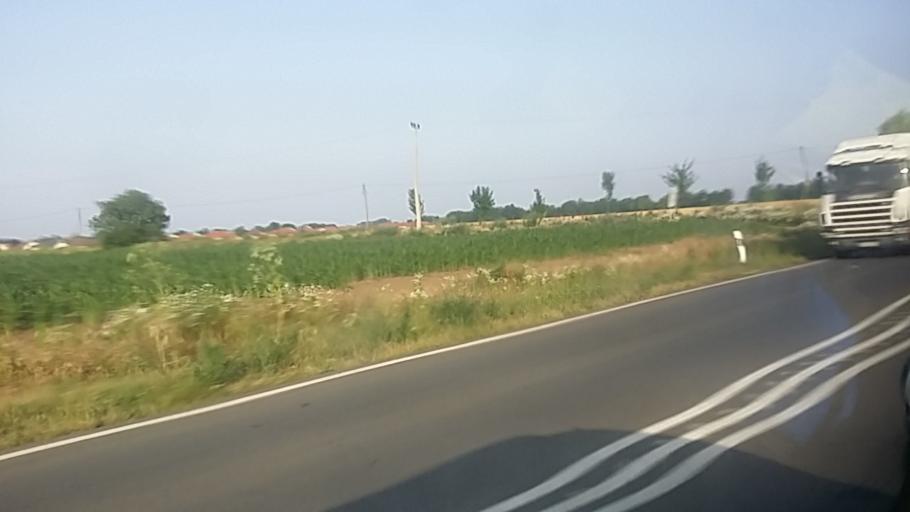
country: HU
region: Baranya
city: Boly
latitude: 45.9602
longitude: 18.5046
